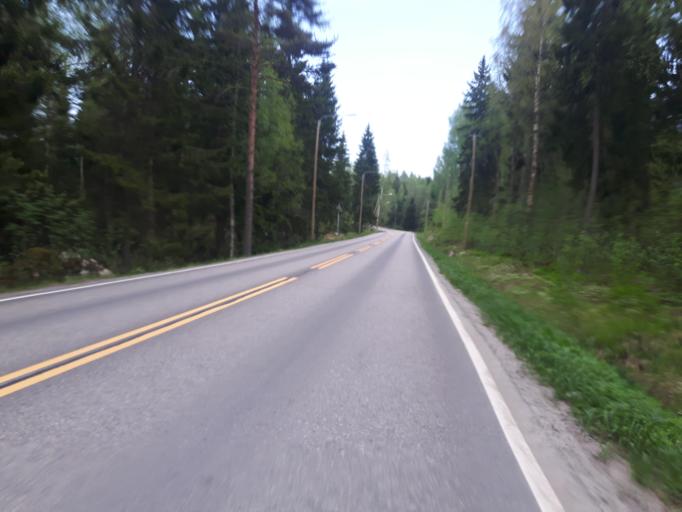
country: FI
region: Uusimaa
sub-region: Porvoo
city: Porvoo
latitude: 60.3900
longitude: 25.7486
